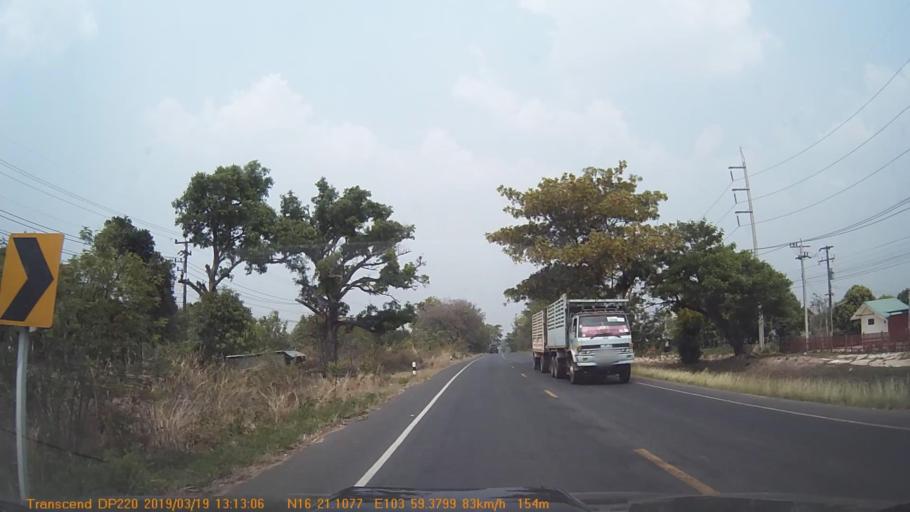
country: TH
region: Roi Et
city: Waeng
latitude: 16.3520
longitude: 103.9898
